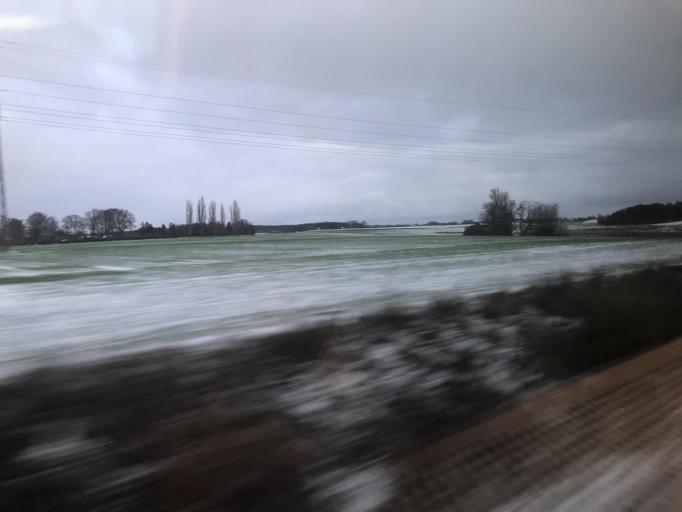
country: SE
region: Skane
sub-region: Landskrona
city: Asmundtorp
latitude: 55.8581
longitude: 12.9310
